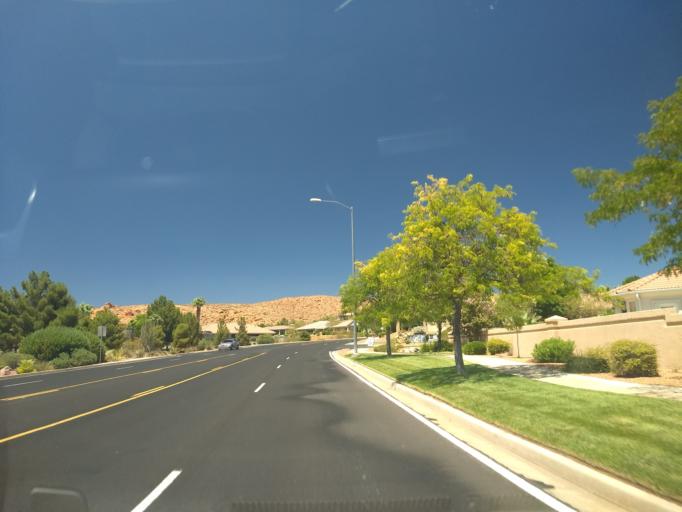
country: US
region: Utah
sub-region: Washington County
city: Washington
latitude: 37.1402
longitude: -113.5277
